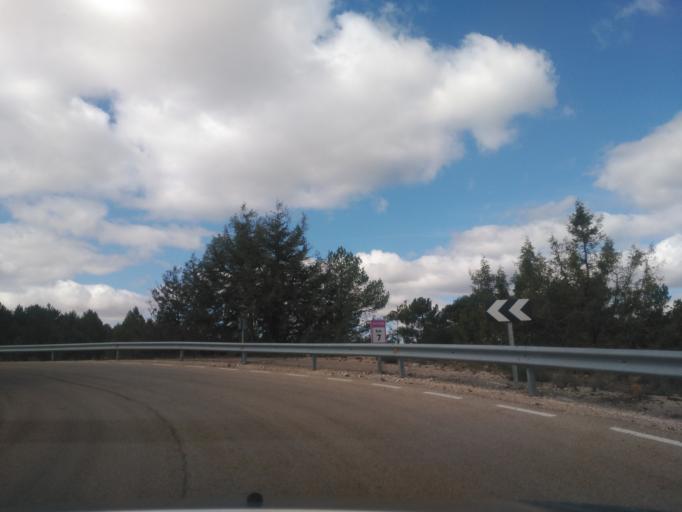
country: ES
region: Castille and Leon
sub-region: Provincia de Soria
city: Espejon
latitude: 41.8410
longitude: -3.2396
